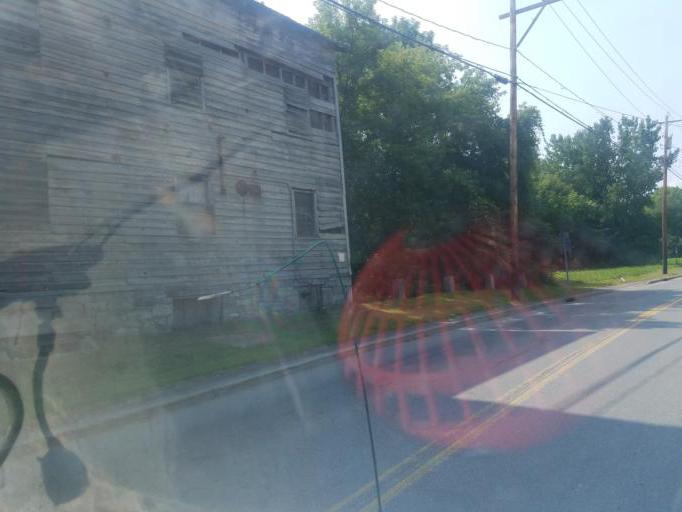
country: US
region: New York
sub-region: Montgomery County
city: Fonda
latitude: 42.9540
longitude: -74.3806
